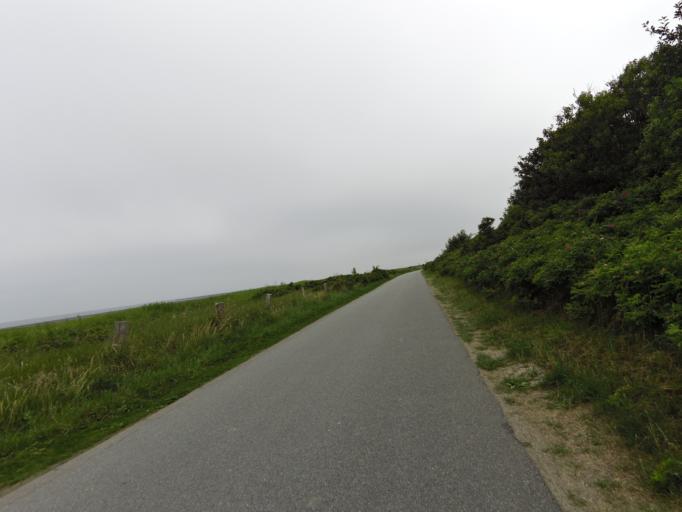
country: DE
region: Lower Saxony
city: Nordholz
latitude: 53.8677
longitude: 8.6012
